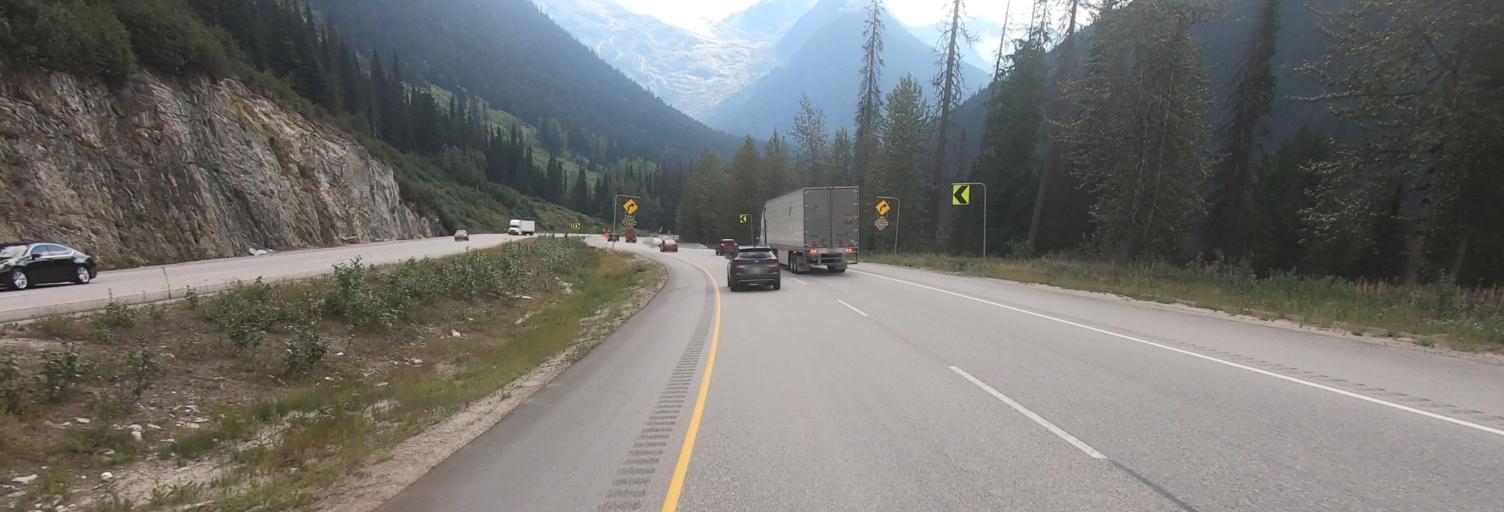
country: CA
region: British Columbia
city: Golden
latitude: 51.2729
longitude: -117.5071
